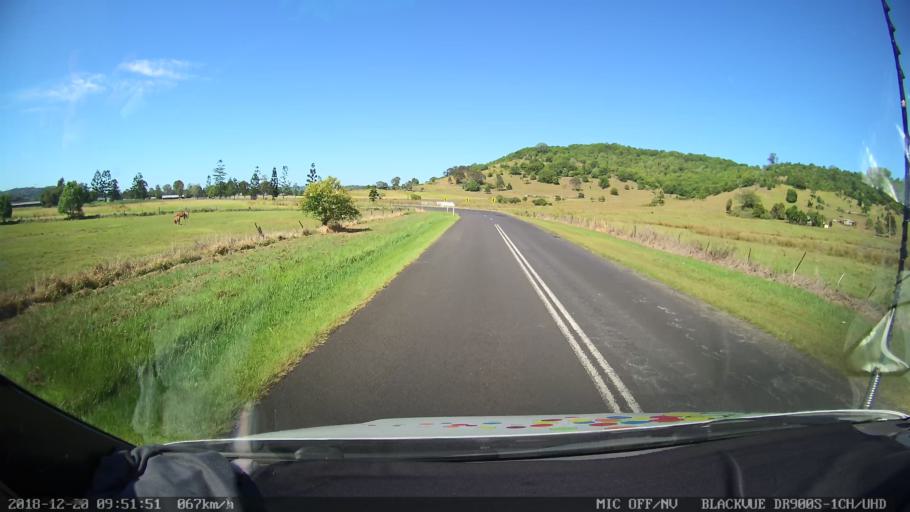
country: AU
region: New South Wales
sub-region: Lismore Municipality
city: Lismore
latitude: -28.7907
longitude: 153.2732
